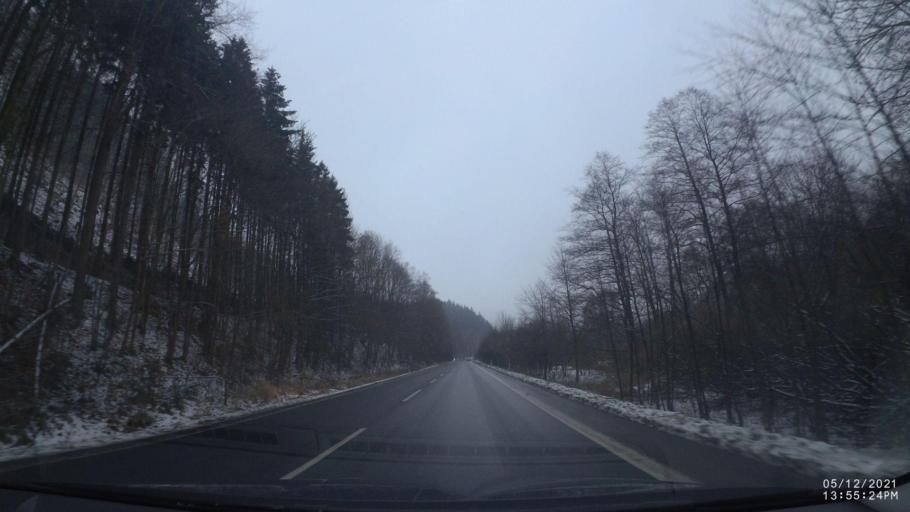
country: CZ
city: Hronov
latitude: 50.4995
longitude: 16.2017
